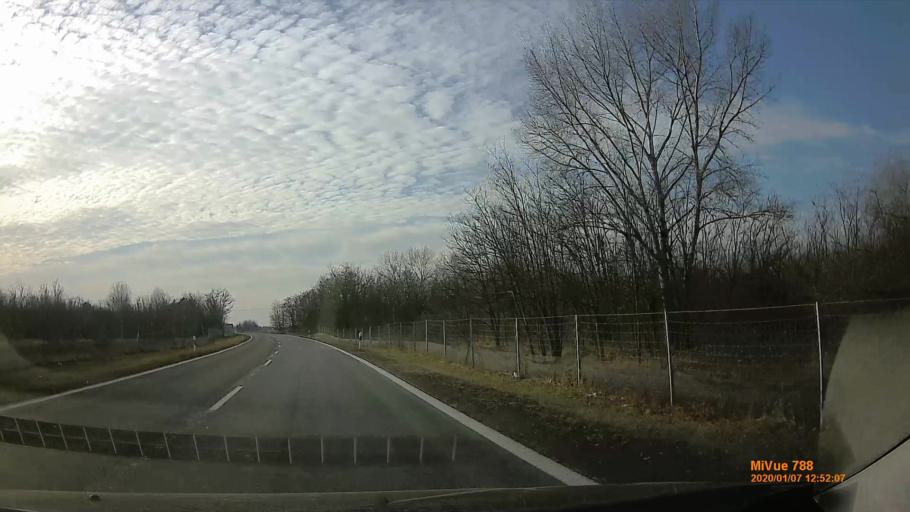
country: HU
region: Gyor-Moson-Sopron
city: Gyor
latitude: 47.7159
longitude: 17.6855
